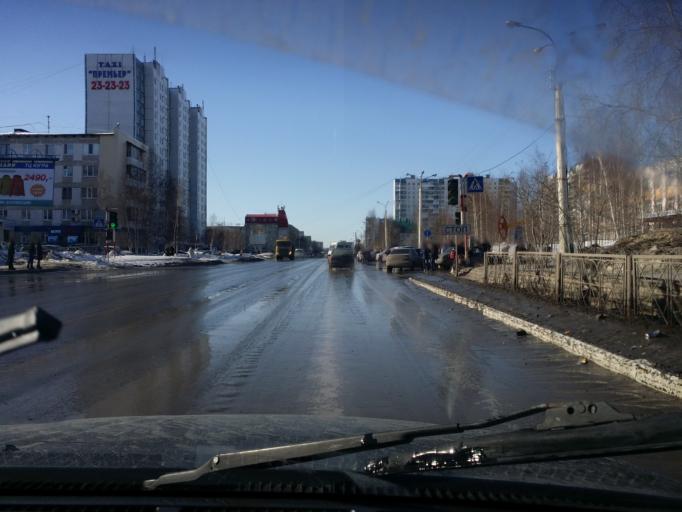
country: RU
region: Khanty-Mansiyskiy Avtonomnyy Okrug
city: Nizhnevartovsk
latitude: 60.9413
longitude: 76.5858
